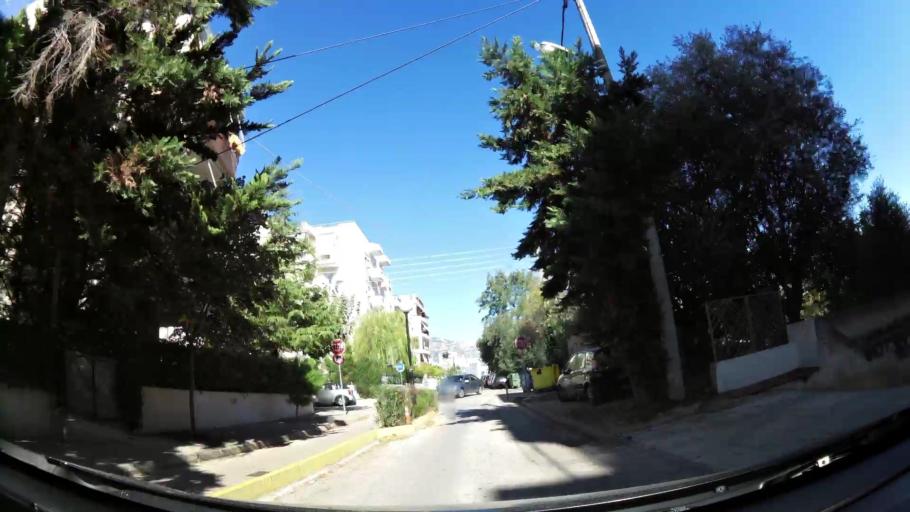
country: GR
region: Attica
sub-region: Nomarchia Athinas
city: Vrilissia
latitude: 38.0256
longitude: 23.8288
